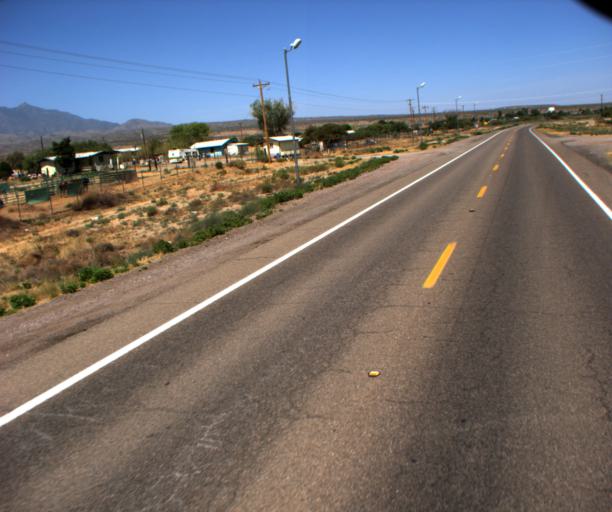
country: US
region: Arizona
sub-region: Graham County
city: Bylas
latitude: 33.1145
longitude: -110.1022
